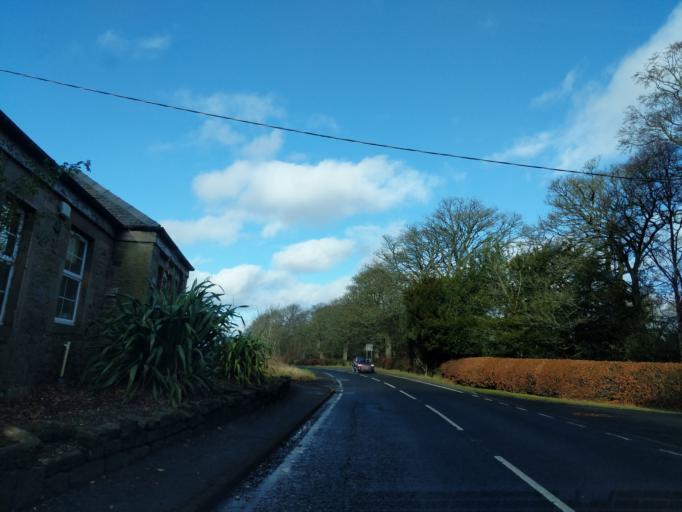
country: GB
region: Scotland
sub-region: West Lothian
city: Kirknewton
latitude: 55.8831
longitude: -3.4202
